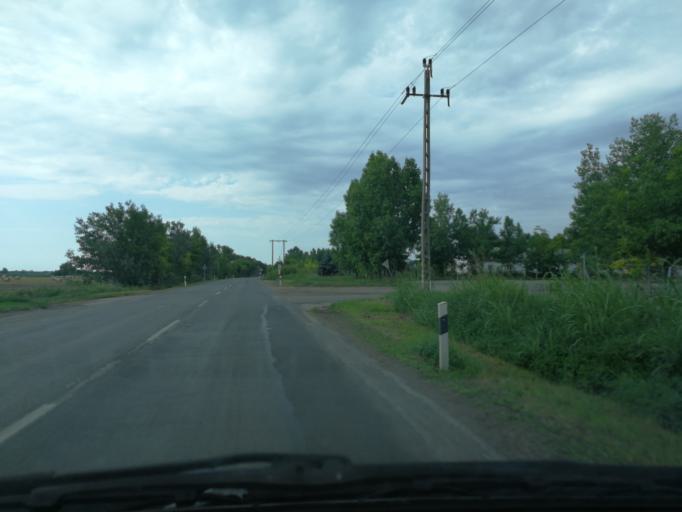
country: HU
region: Bacs-Kiskun
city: Dusnok
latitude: 46.3660
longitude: 18.9634
